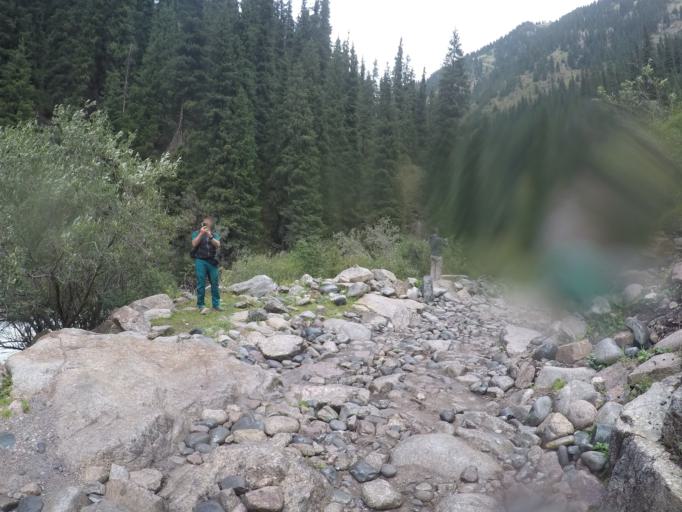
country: KG
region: Ysyk-Koel
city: Teploklyuchenka
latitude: 42.4157
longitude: 78.5713
